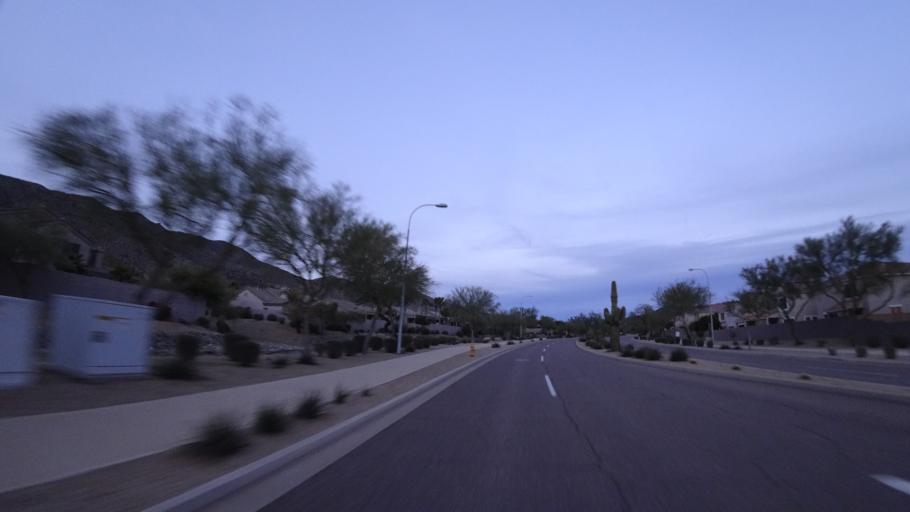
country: US
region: Arizona
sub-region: Maricopa County
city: Laveen
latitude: 33.3113
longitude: -112.0795
